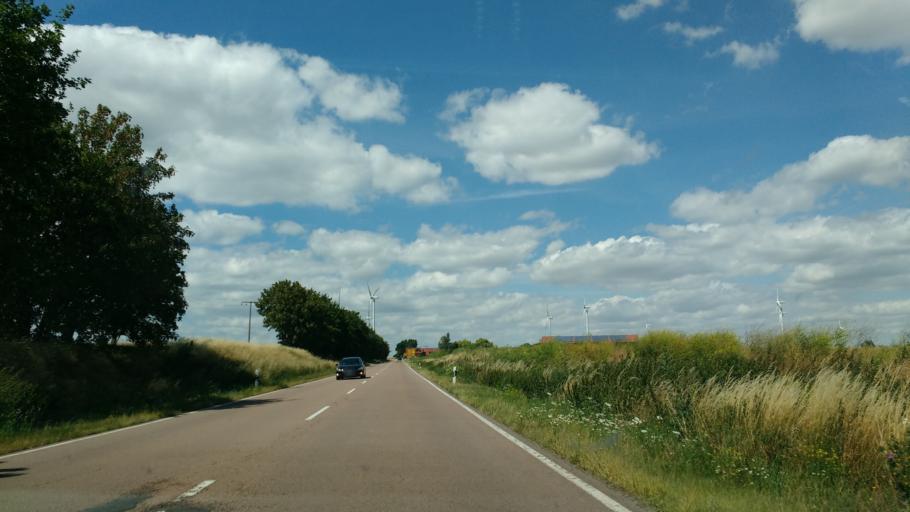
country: DE
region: Saxony-Anhalt
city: Querfurt
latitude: 51.3986
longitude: 11.5891
